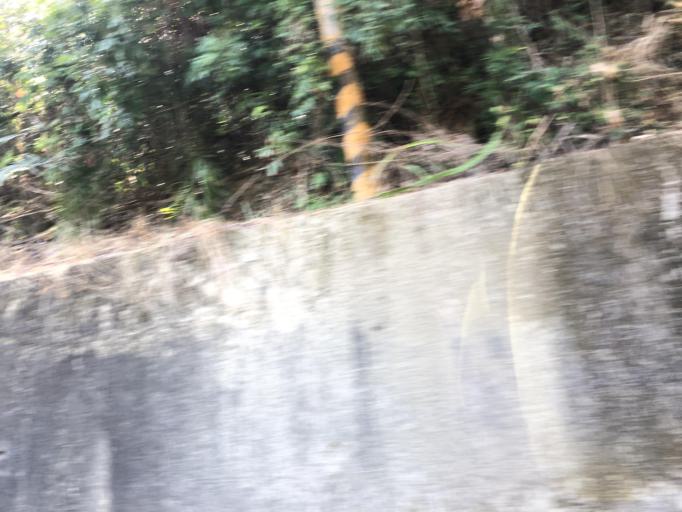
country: TW
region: Taiwan
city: Yujing
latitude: 23.0309
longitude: 120.3932
